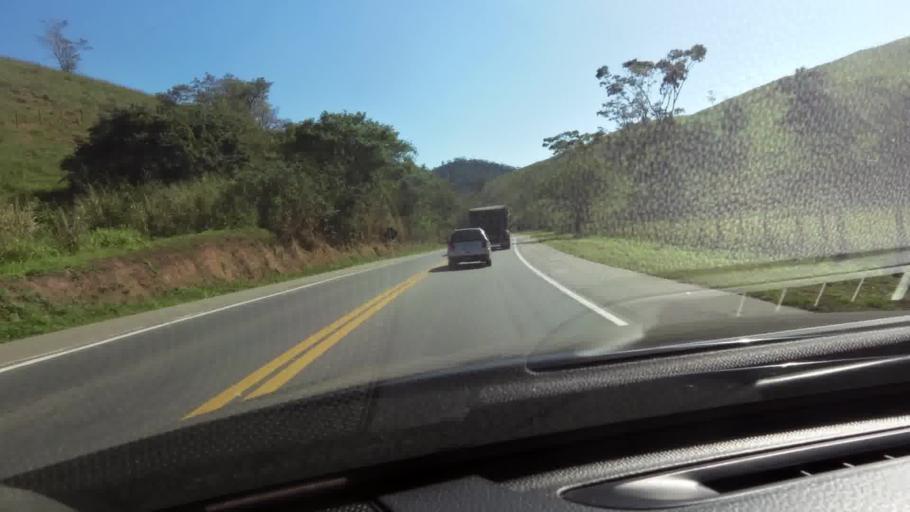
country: BR
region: Espirito Santo
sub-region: Rio Novo Do Sul
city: Rio Novo do Sul
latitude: -20.8970
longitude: -41.0249
